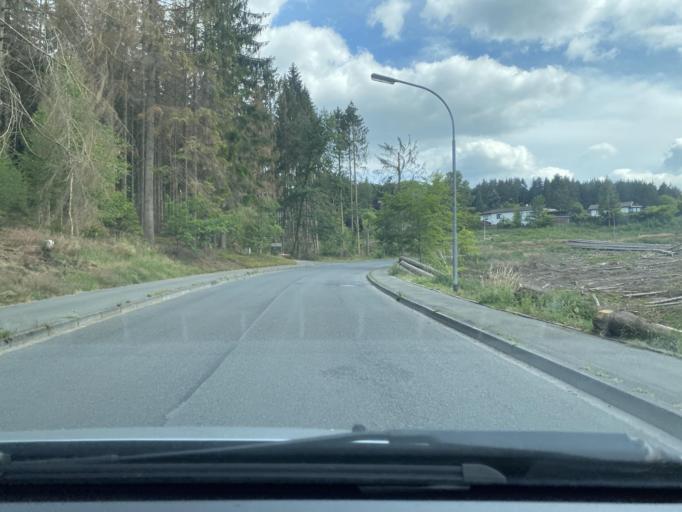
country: DE
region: North Rhine-Westphalia
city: Werdohl
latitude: 51.2508
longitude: 7.7791
